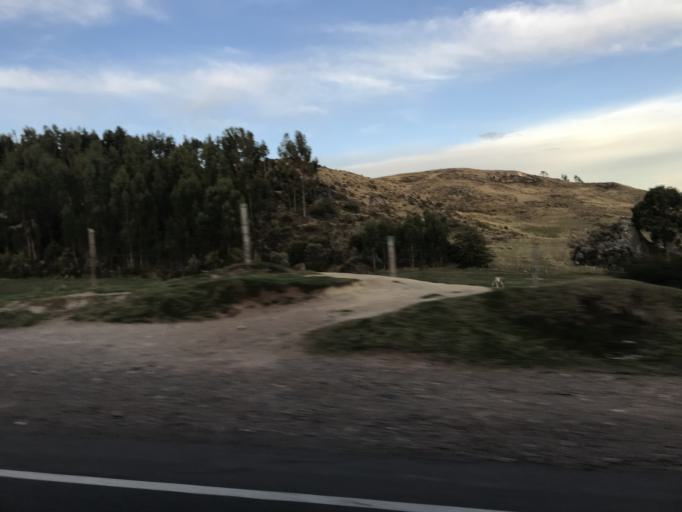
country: PE
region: Cusco
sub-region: Provincia de Cusco
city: Cusco
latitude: -13.4967
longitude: -71.9729
